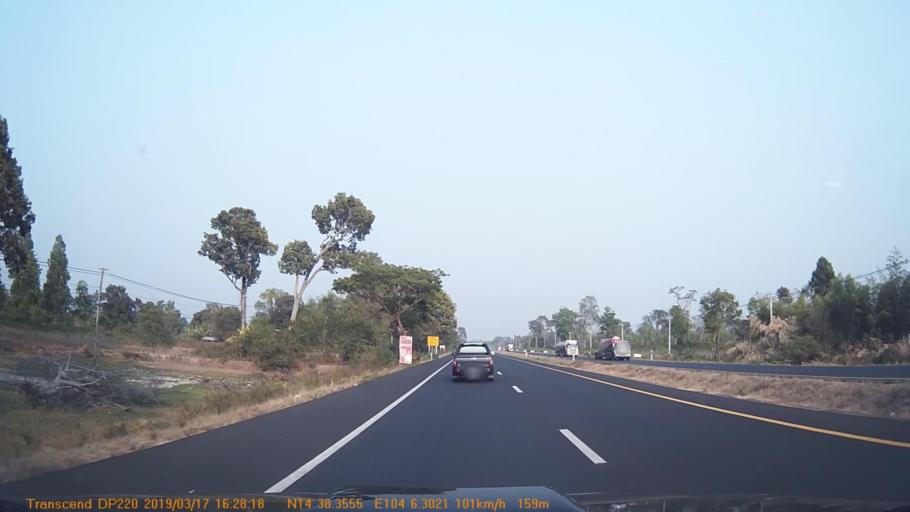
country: TH
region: Sisaket
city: Phu Sing
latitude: 14.6392
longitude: 104.1056
